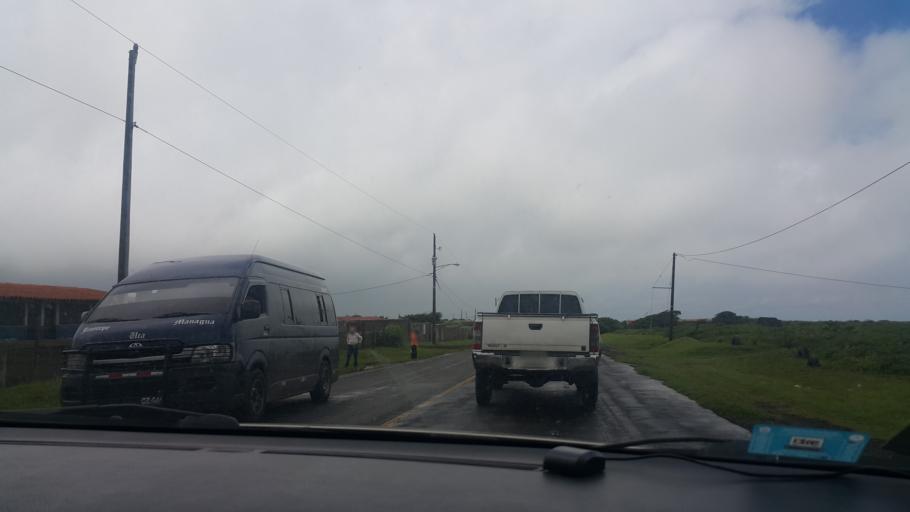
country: NI
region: Managua
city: El Crucero
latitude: 11.9489
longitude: -86.3006
